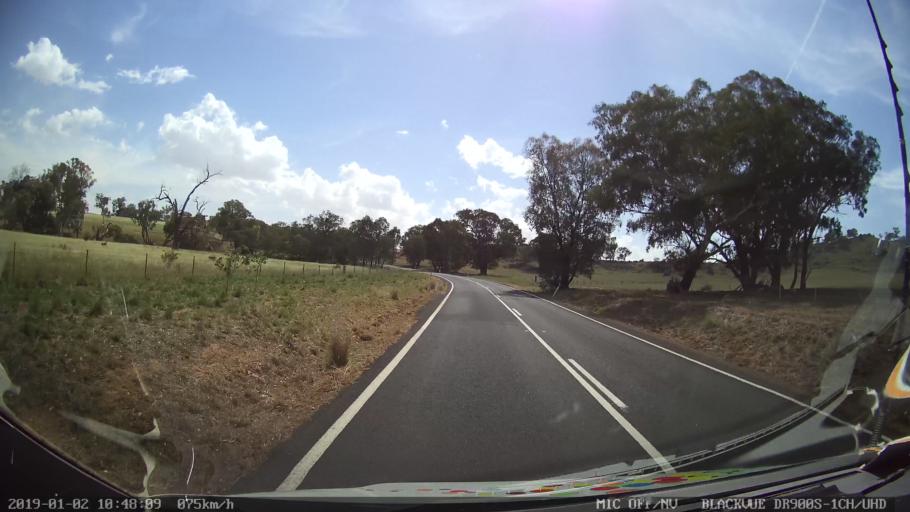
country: AU
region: New South Wales
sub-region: Cootamundra
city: Cootamundra
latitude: -34.7391
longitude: 148.2758
